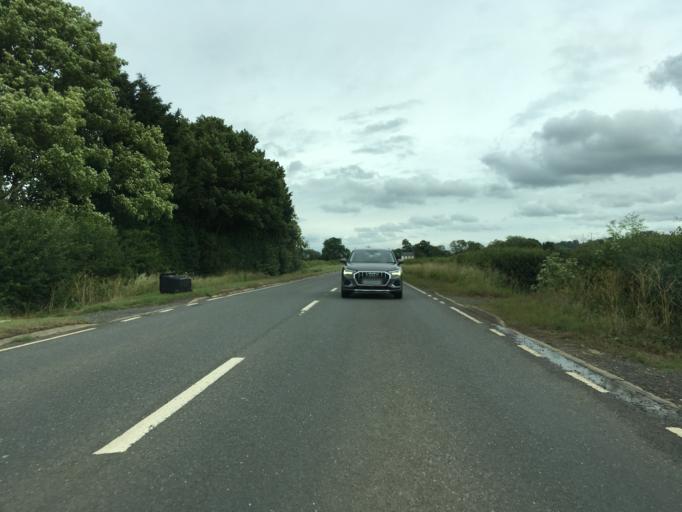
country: GB
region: England
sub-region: Warwickshire
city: Southam
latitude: 52.2530
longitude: -1.3647
